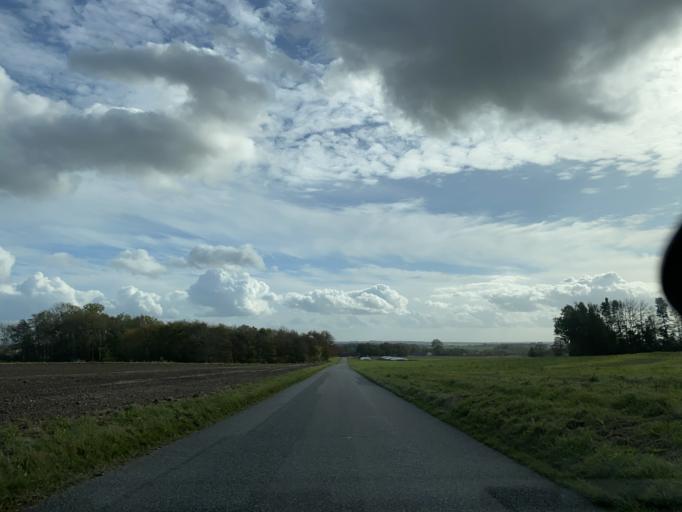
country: DK
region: Central Jutland
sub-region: Arhus Kommune
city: Sabro
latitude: 56.1984
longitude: 9.9992
